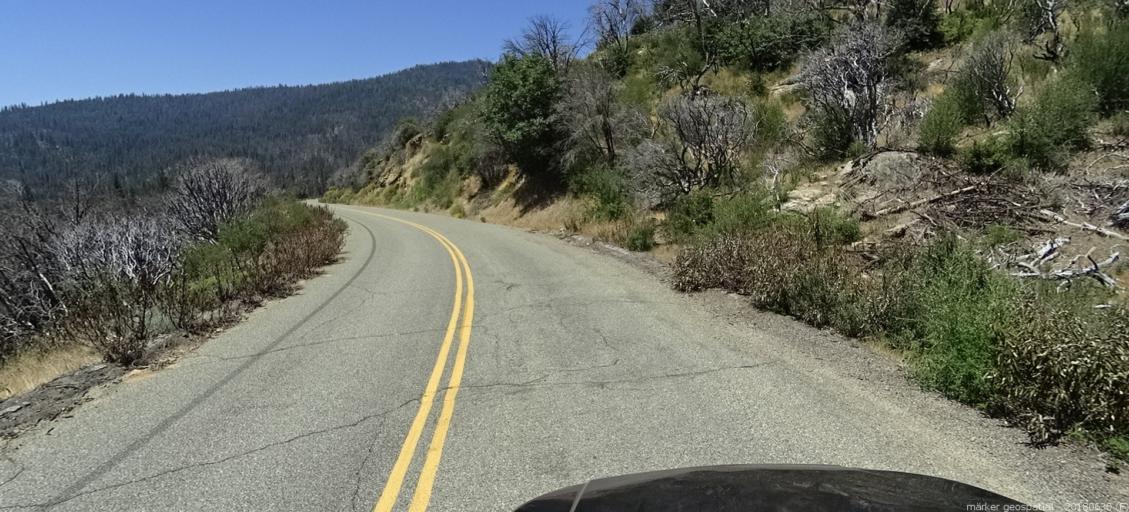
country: US
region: California
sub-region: Fresno County
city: Auberry
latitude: 37.3002
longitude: -119.3595
